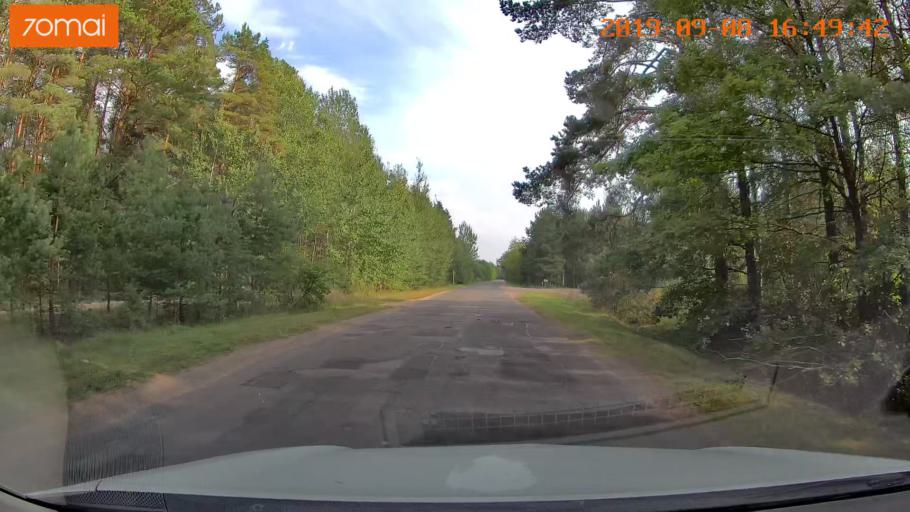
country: BY
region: Grodnenskaya
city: Hrodna
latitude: 53.8080
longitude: 23.8782
